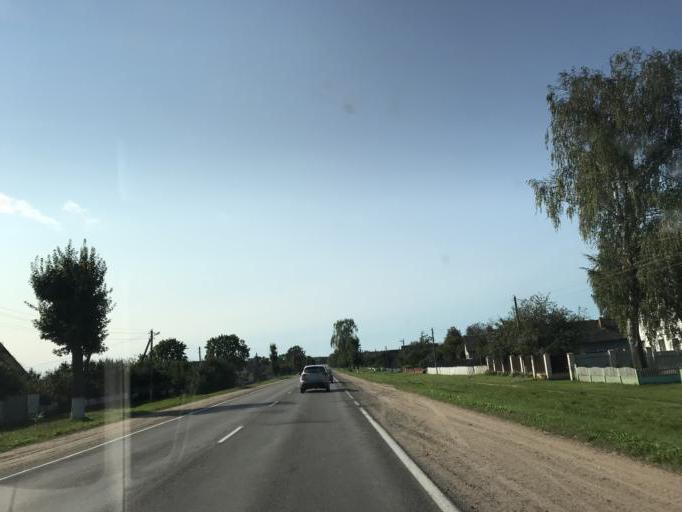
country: BY
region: Mogilev
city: Buynichy
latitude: 53.8359
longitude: 30.2462
